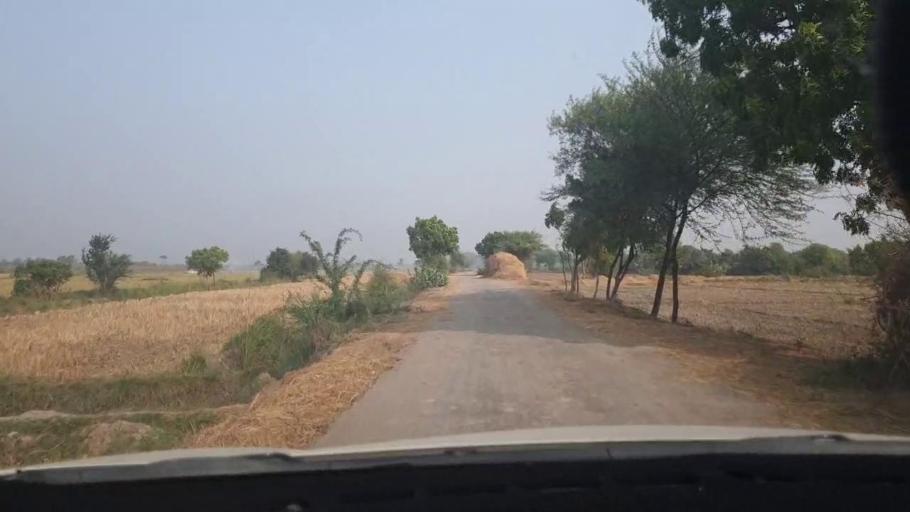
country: PK
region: Sindh
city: Tando Muhammad Khan
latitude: 24.9712
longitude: 68.4867
